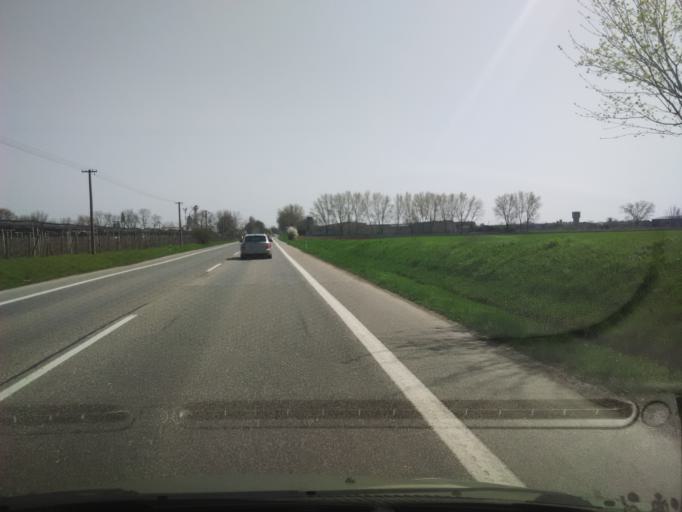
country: SK
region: Nitriansky
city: Surany
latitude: 48.1089
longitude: 18.0502
